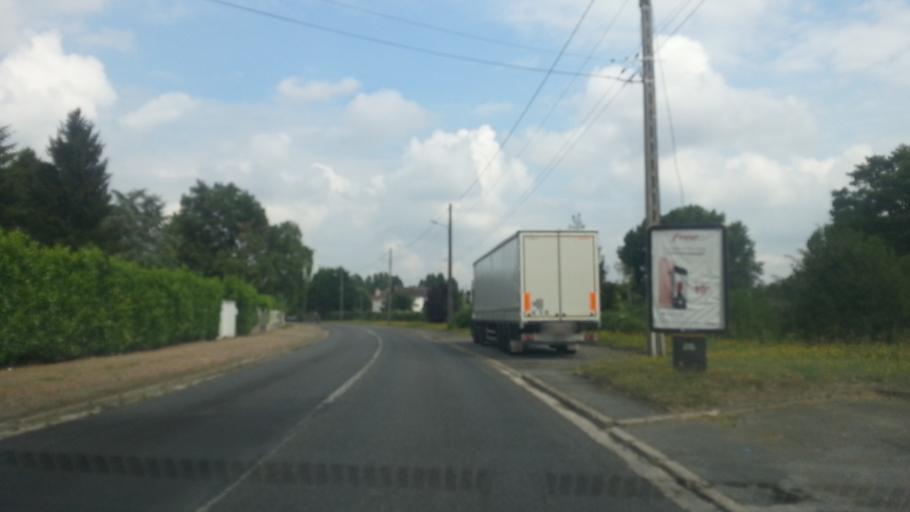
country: FR
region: Picardie
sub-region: Departement de l'Oise
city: Saint-Maximin
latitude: 49.2177
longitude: 2.4246
